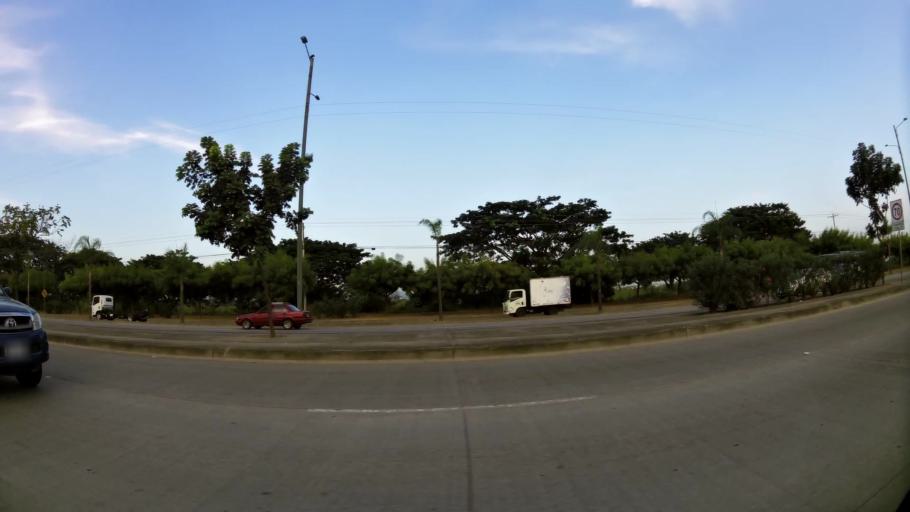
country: EC
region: Guayas
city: Eloy Alfaro
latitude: -2.1043
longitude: -79.8881
